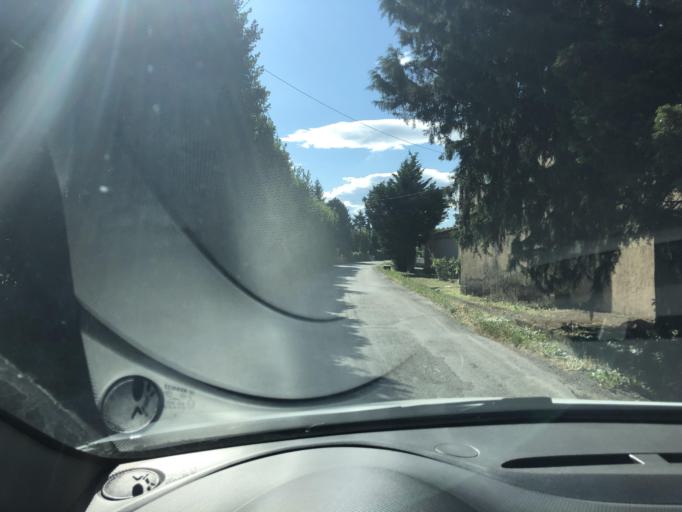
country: FR
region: Provence-Alpes-Cote d'Azur
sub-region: Departement des Bouches-du-Rhone
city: Rognonas
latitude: 43.9049
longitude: 4.8278
